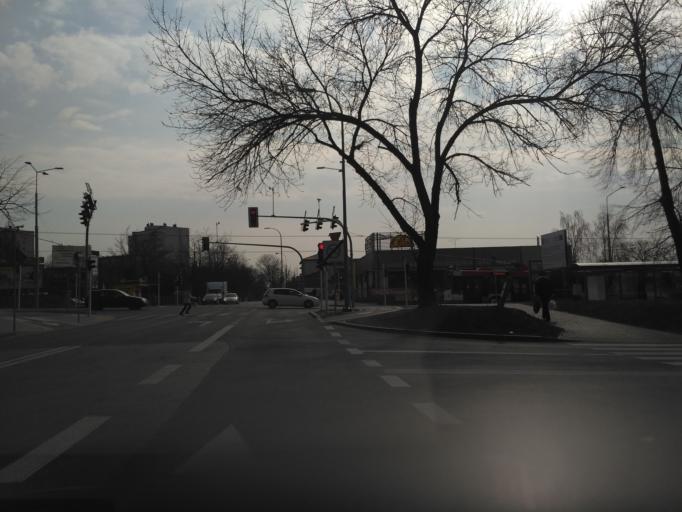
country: PL
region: Lublin Voivodeship
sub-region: Powiat lubelski
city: Lublin
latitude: 51.2335
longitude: 22.5866
